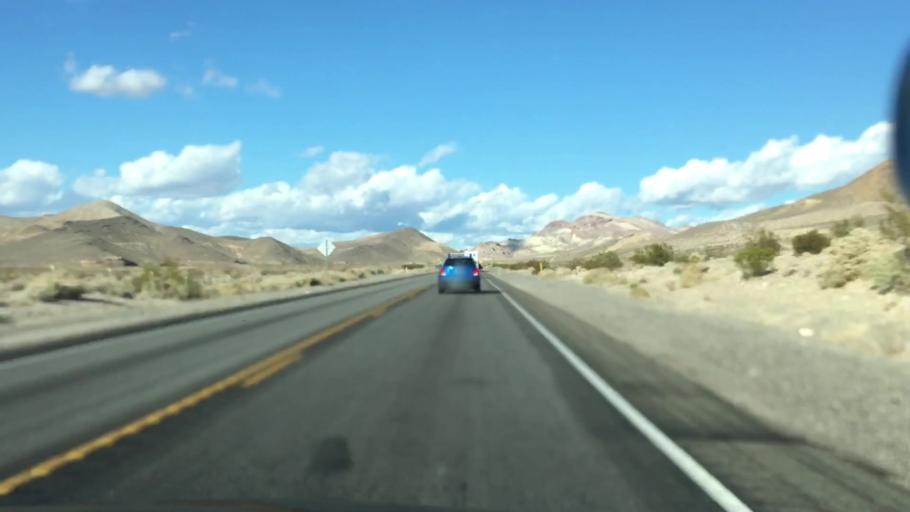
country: US
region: Nevada
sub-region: Nye County
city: Beatty
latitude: 36.8607
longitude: -116.7572
